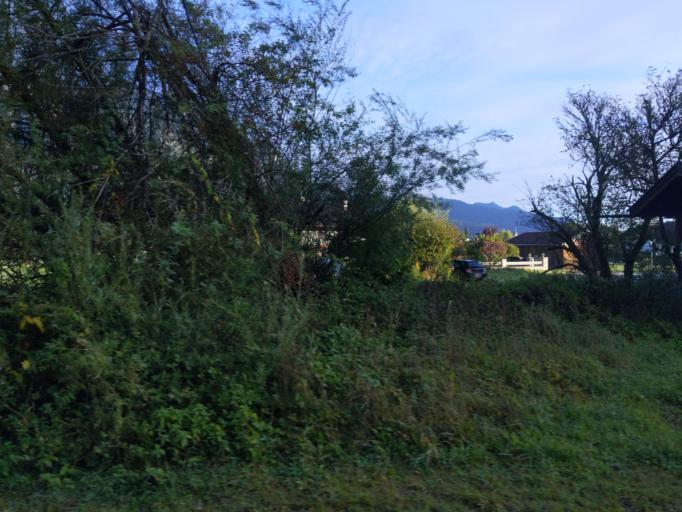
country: DE
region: Bavaria
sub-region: Upper Bavaria
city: Garmisch-Partenkirchen
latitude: 47.4816
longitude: 11.0820
